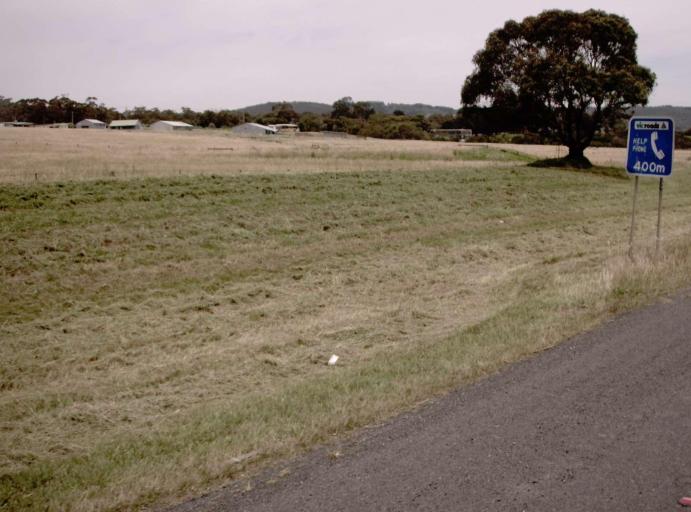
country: AU
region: Victoria
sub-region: Mornington Peninsula
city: Safety Beach
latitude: -38.3134
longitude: 145.0159
